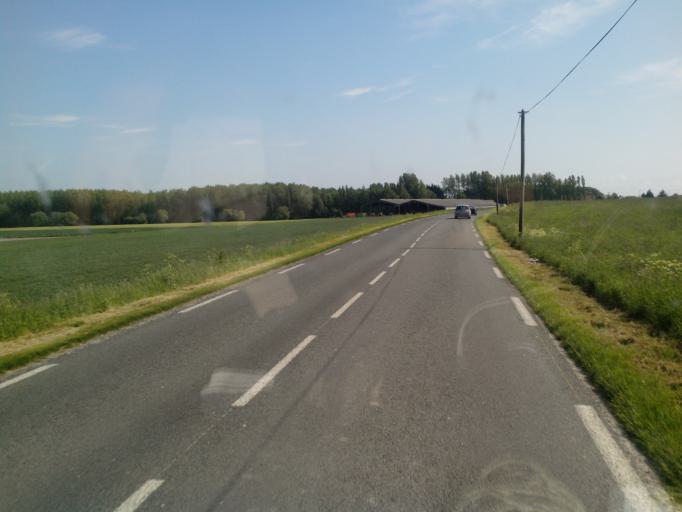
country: FR
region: Picardie
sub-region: Departement de la Somme
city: Quend
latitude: 50.3338
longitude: 1.6439
